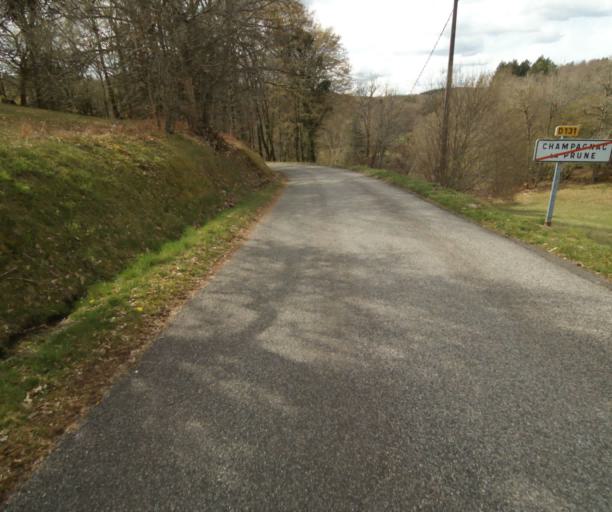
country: FR
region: Limousin
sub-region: Departement de la Correze
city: Argentat
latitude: 45.1857
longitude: 1.9486
